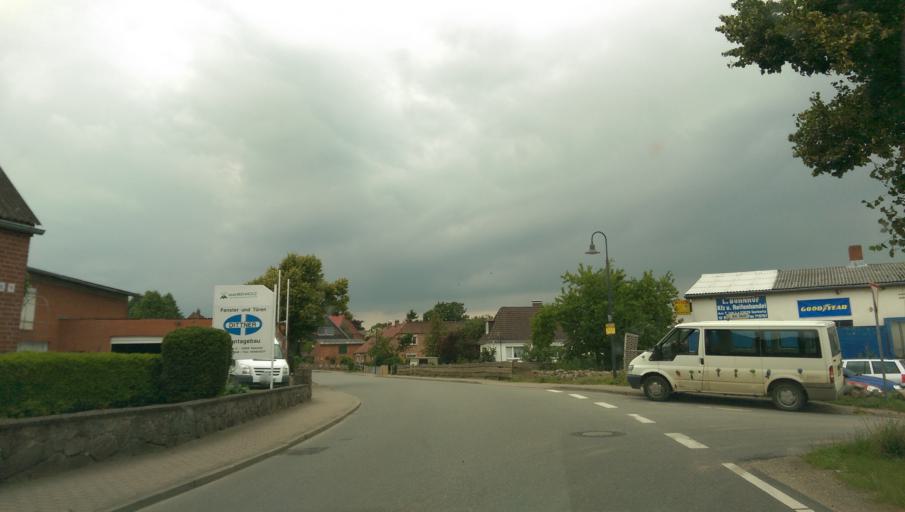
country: DE
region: Schleswig-Holstein
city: Ratekau
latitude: 53.9910
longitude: 10.6680
